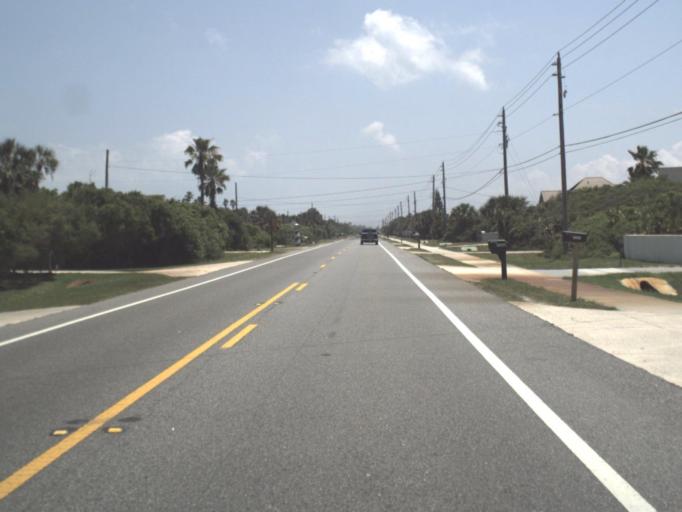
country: US
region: Florida
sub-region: Saint Johns County
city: Butler Beach
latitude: 29.7591
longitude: -81.2498
